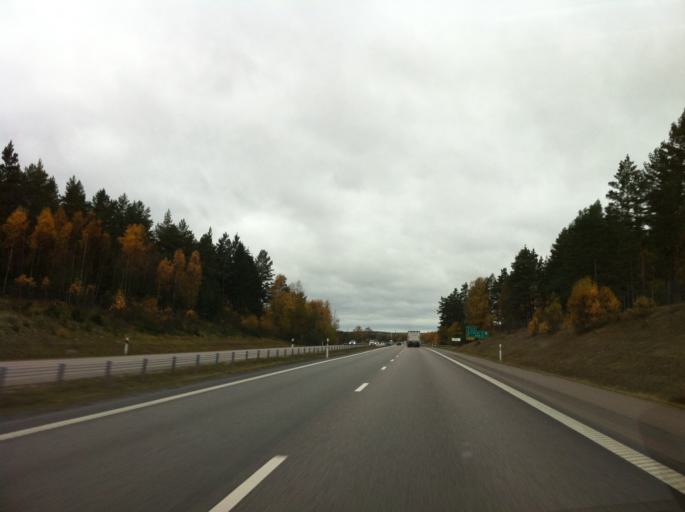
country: SE
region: OEstergoetland
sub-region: Mjolby Kommun
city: Mjolby
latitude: 58.3487
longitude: 15.1926
